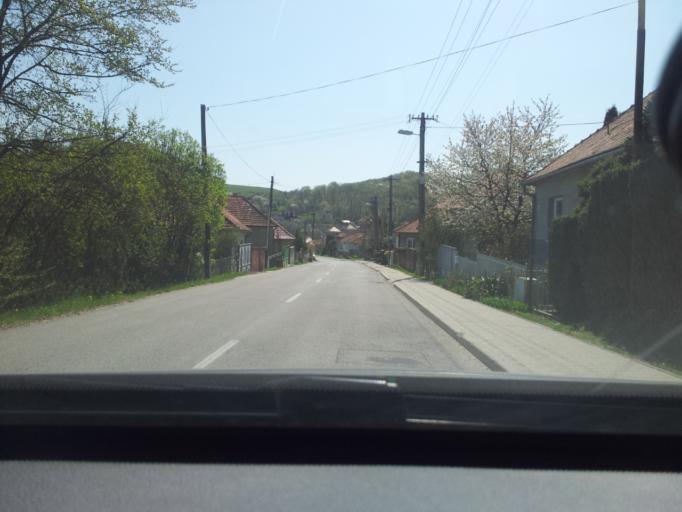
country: SK
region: Nitriansky
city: Zlate Moravce
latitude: 48.5034
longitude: 18.4213
